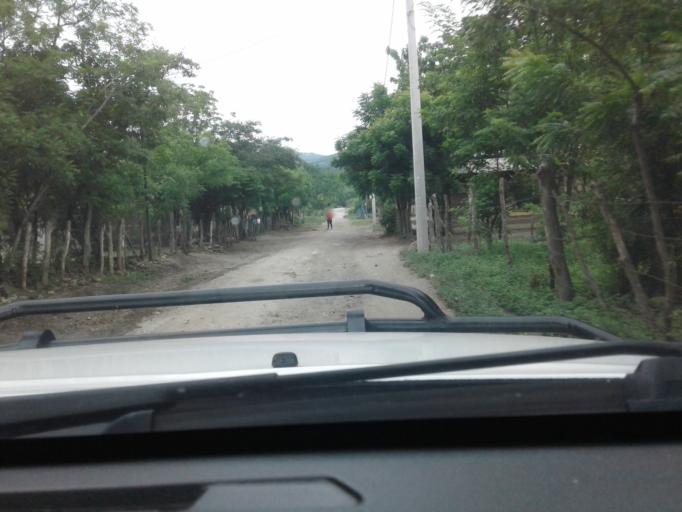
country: NI
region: Matagalpa
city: Ciudad Dario
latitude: 12.9023
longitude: -86.2032
